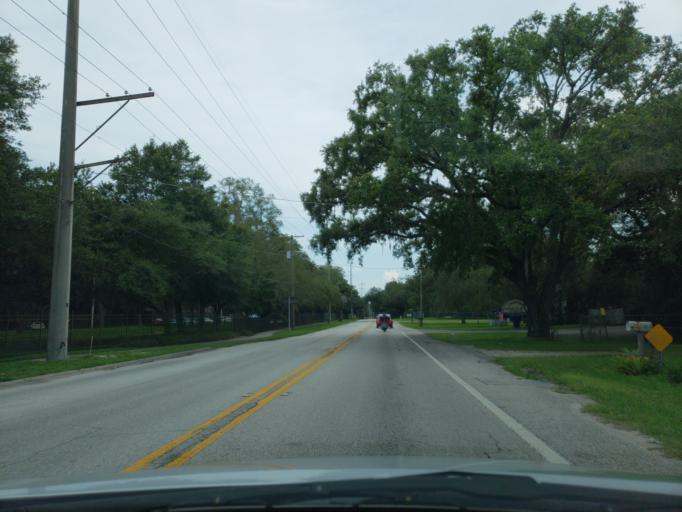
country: US
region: Florida
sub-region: Hillsborough County
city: University
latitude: 28.0898
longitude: -82.4308
